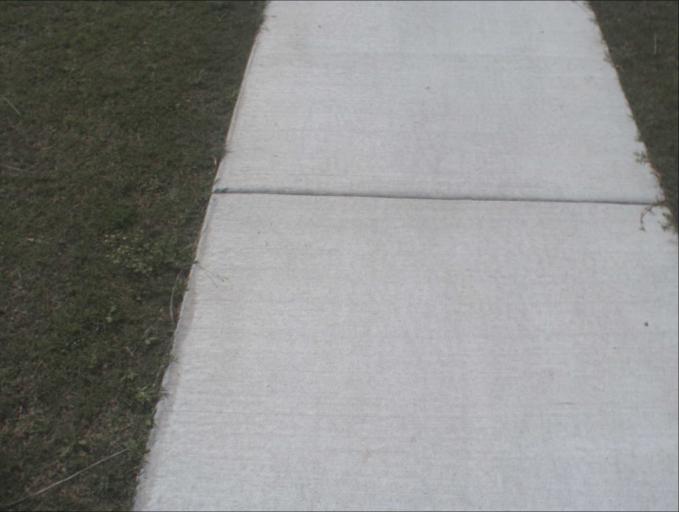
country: AU
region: Queensland
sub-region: Logan
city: Park Ridge South
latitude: -27.6762
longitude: 153.0348
